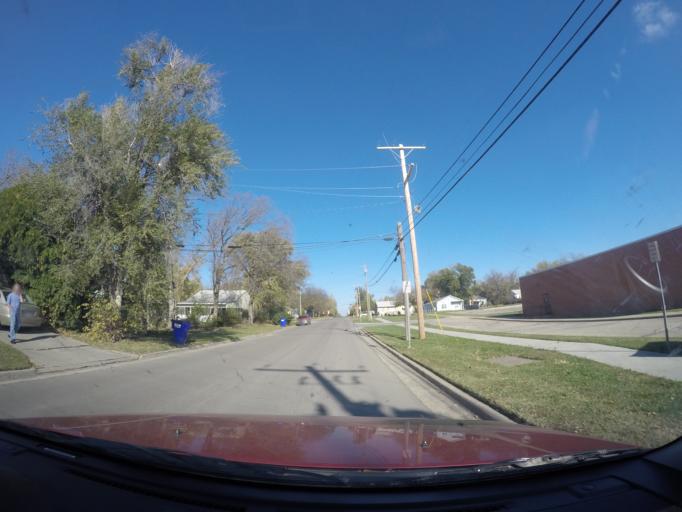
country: US
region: Kansas
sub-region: Geary County
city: Junction City
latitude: 39.0150
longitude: -96.8371
